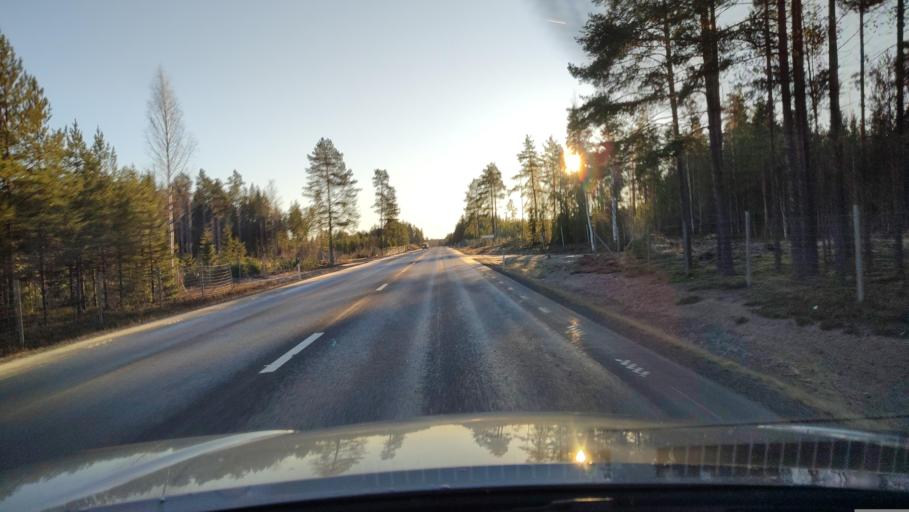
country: SE
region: Vaesterbotten
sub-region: Skelleftea Kommun
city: Burea
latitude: 64.5970
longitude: 21.2077
